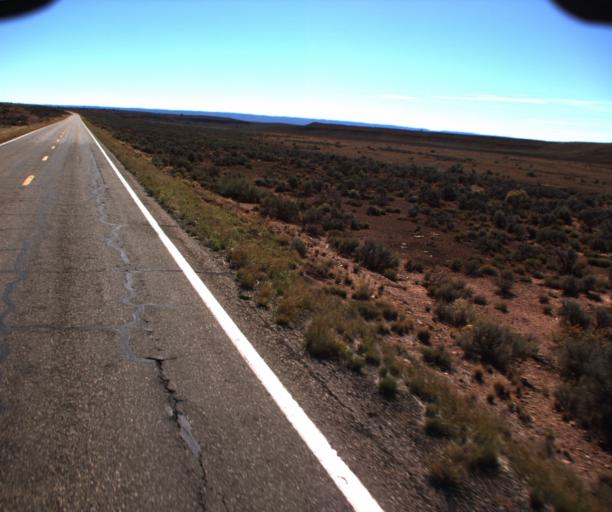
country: US
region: Arizona
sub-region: Coconino County
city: Fredonia
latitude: 36.9143
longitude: -112.4246
